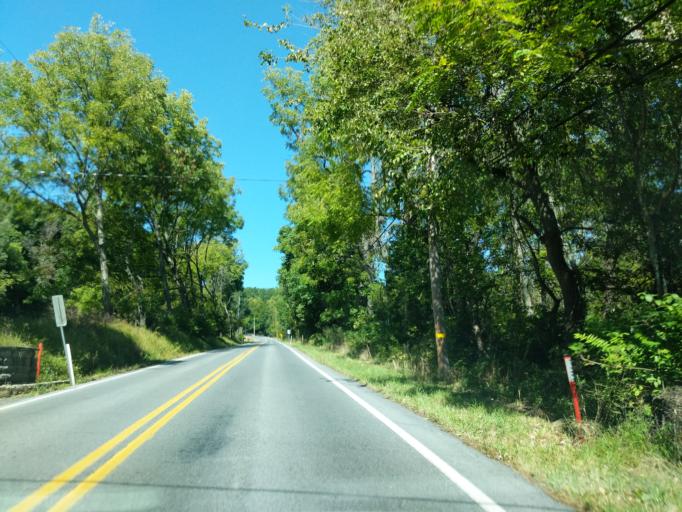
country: US
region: Pennsylvania
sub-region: Montgomery County
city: East Greenville
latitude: 40.4379
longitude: -75.4863
